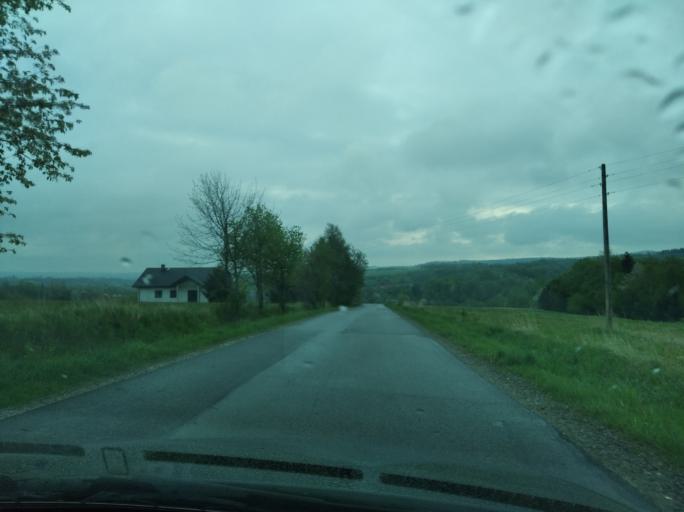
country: PL
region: Subcarpathian Voivodeship
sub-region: Powiat rzeszowski
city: Straszydle
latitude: 49.8768
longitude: 21.9862
